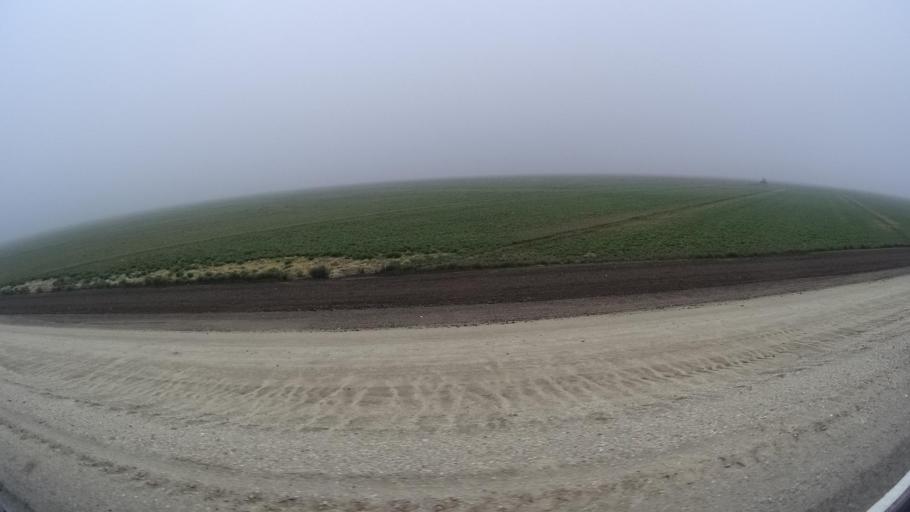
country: US
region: California
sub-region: Kern County
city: Buttonwillow
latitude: 35.4361
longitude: -119.5459
